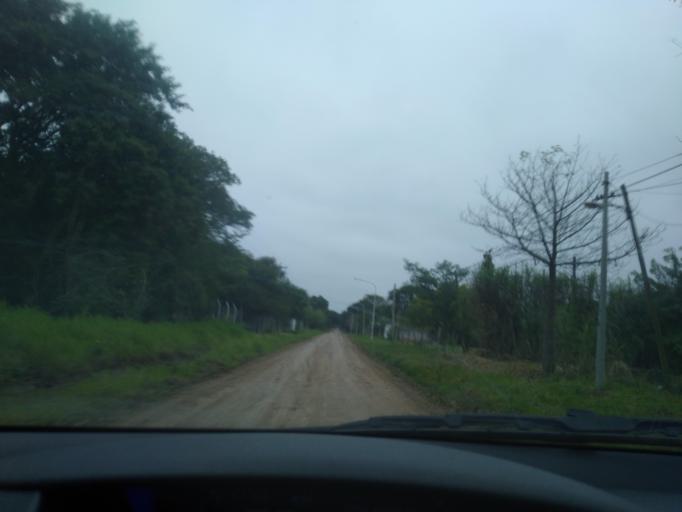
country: AR
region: Chaco
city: Colonia Benitez
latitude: -27.3334
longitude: -58.9602
